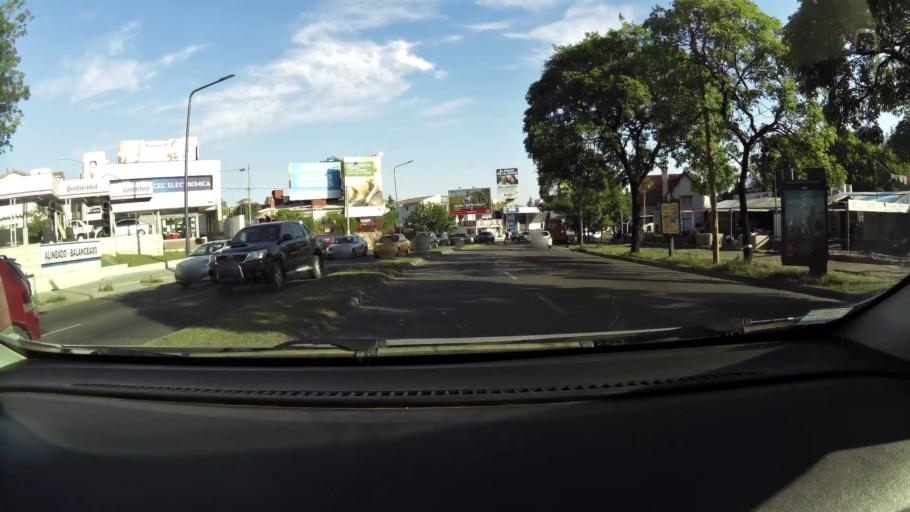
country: AR
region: Cordoba
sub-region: Departamento de Capital
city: Cordoba
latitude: -31.3797
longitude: -64.2234
